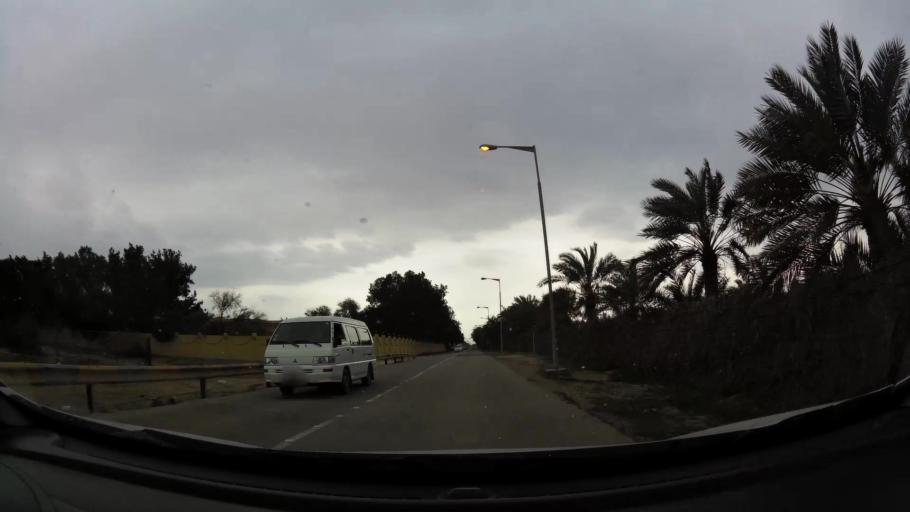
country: BH
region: Central Governorate
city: Madinat Hamad
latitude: 26.1543
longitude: 50.4629
